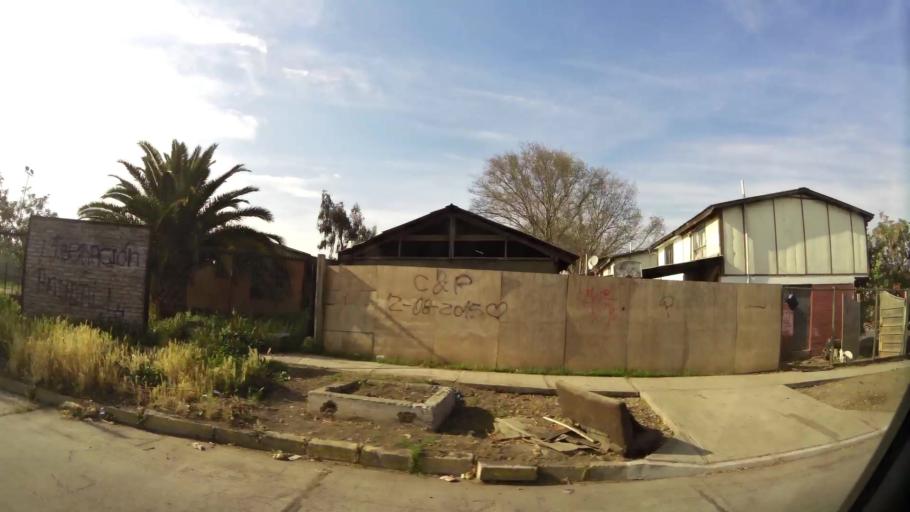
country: CL
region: Santiago Metropolitan
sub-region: Provincia de Talagante
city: Talagante
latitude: -33.6721
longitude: -70.9373
